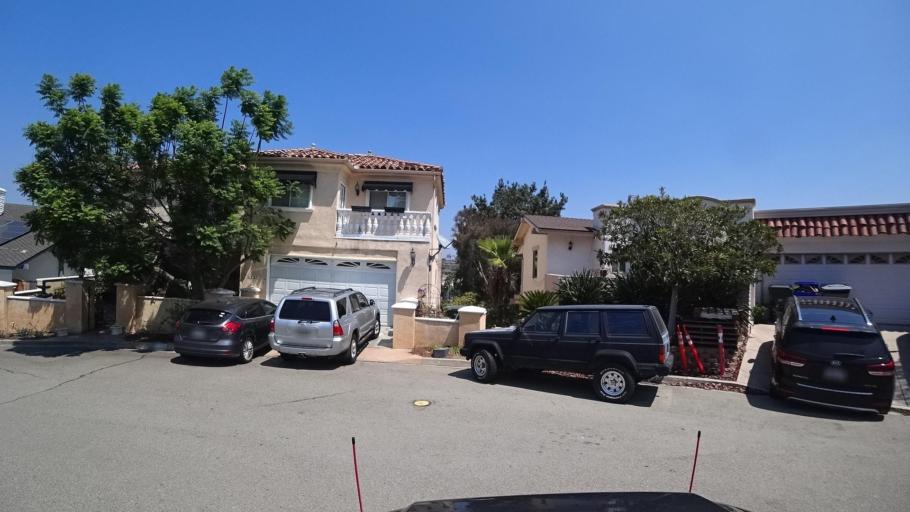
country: US
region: California
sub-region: San Diego County
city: Bonsall
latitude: 33.2861
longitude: -117.2118
